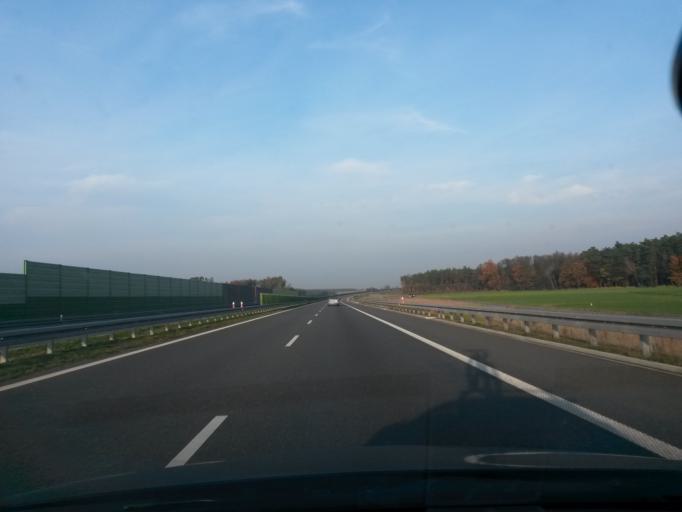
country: PL
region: Lower Silesian Voivodeship
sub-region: Powiat olesnicki
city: Twardogora
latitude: 51.2920
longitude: 17.5800
